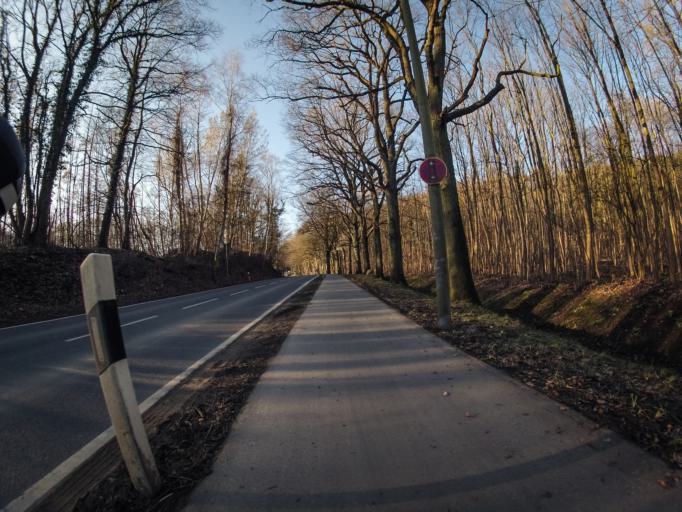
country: DE
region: Lower Saxony
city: Wallenhorst
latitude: 52.3127
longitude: 8.0128
